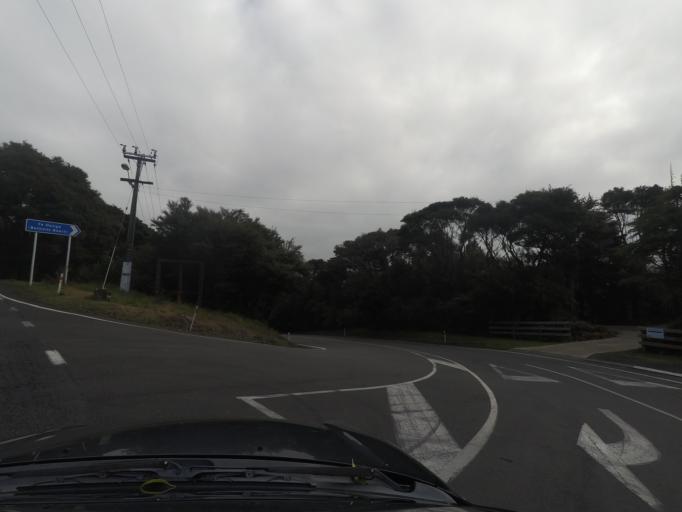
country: NZ
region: Auckland
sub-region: Auckland
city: Muriwai Beach
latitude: -36.8784
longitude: 174.5415
